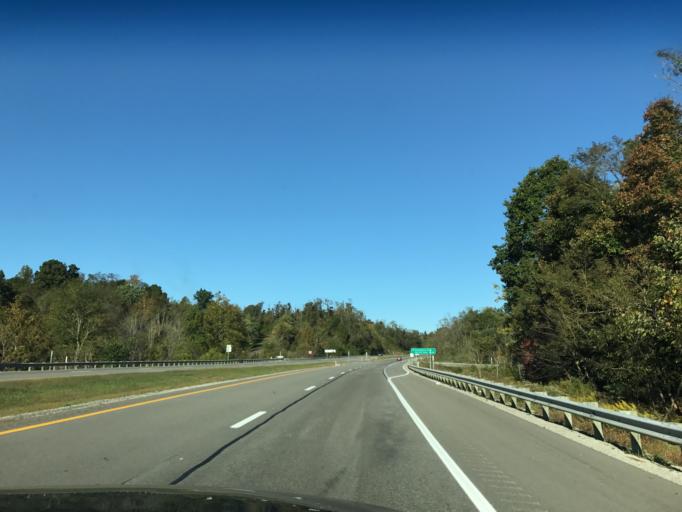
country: US
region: West Virginia
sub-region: Wood County
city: Mineral Wells
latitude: 39.2389
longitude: -81.4607
